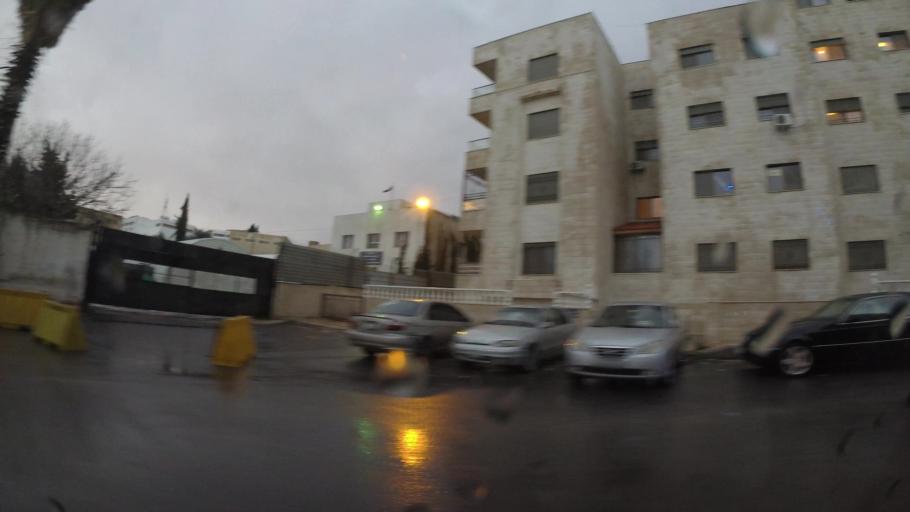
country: JO
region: Amman
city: Amman
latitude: 31.9964
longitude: 35.9285
